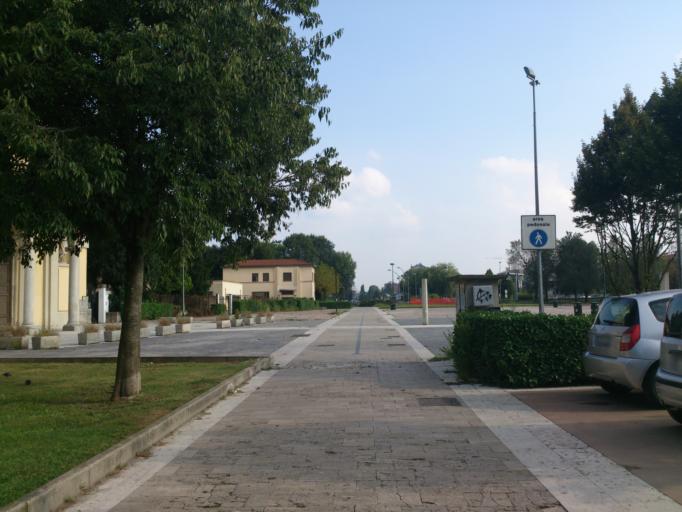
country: IT
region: Lombardy
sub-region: Citta metropolitana di Milano
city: San Donato Milanese
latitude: 45.4149
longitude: 9.2632
